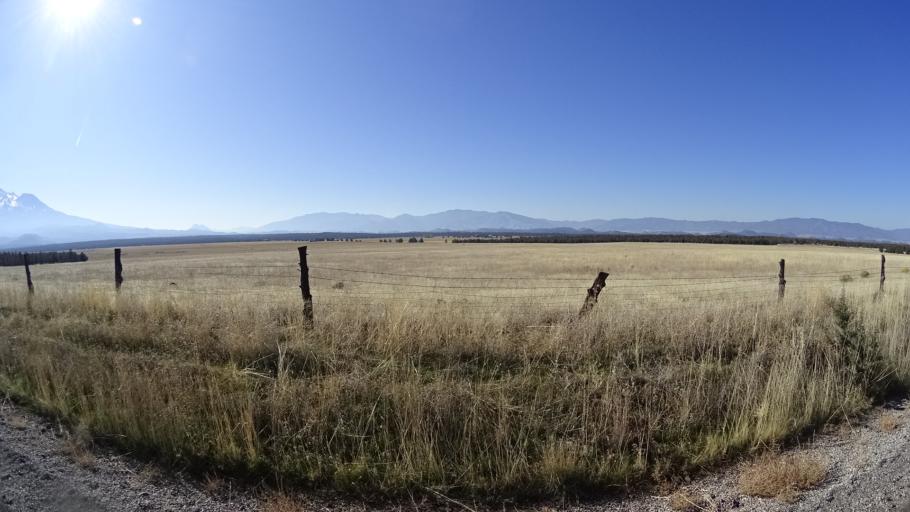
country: US
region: California
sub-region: Siskiyou County
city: Weed
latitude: 41.6127
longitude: -122.3147
